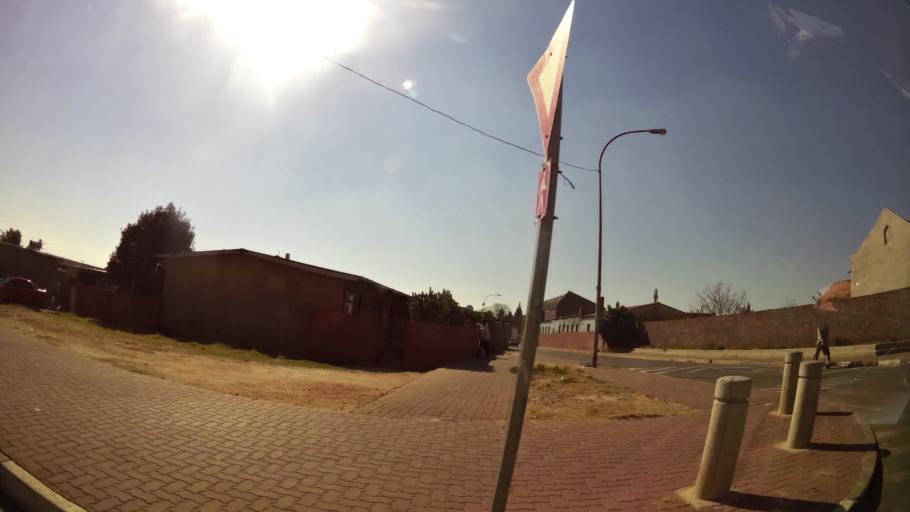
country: ZA
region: Gauteng
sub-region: City of Johannesburg Metropolitan Municipality
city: Johannesburg
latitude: -26.1838
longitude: 27.9724
